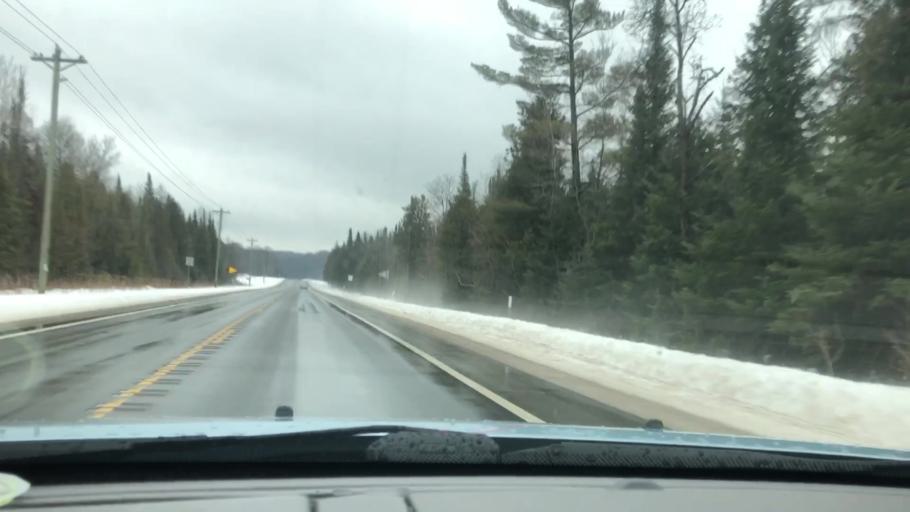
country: US
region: Michigan
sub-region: Charlevoix County
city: Boyne City
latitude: 45.0911
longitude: -84.9465
